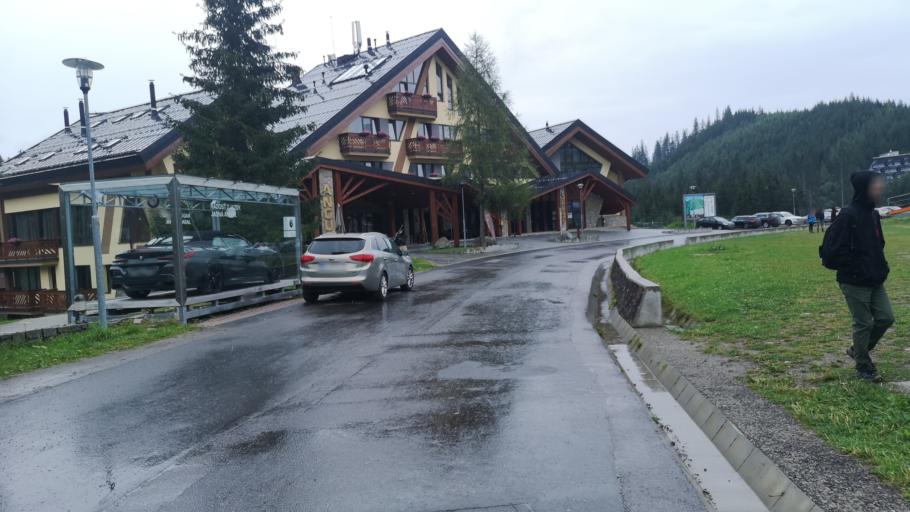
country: SK
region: Zilinsky
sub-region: Okres Liptovsky Mikulas
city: Liptovsky Mikulas
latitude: 48.9707
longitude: 19.5811
